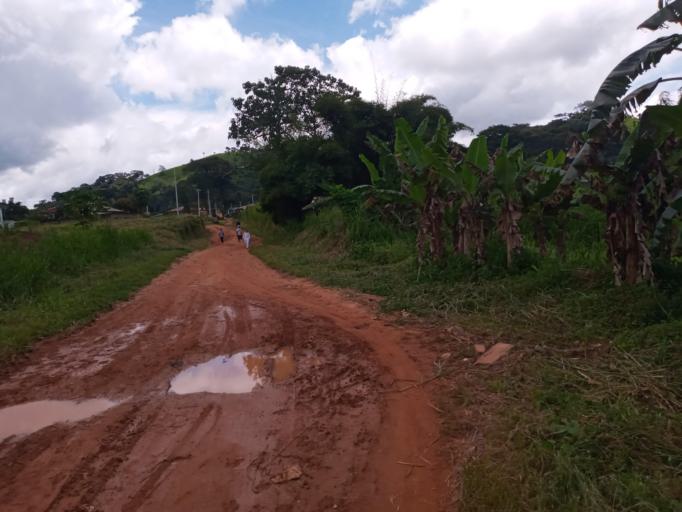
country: SL
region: Eastern Province
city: Tombu
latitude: 8.6267
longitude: -10.8252
